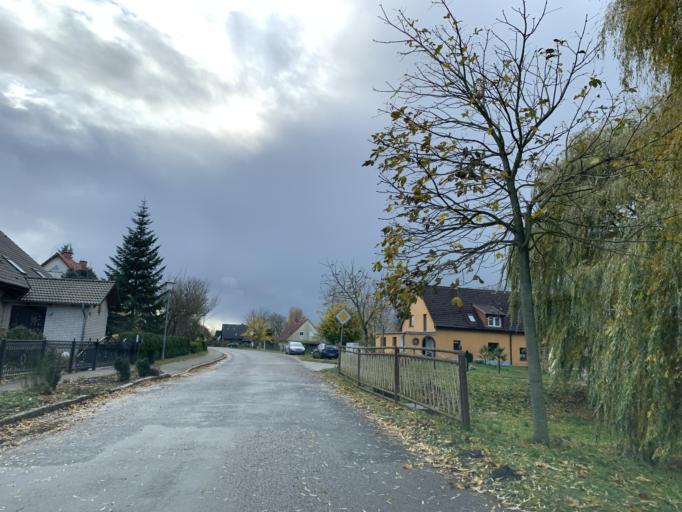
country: DE
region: Mecklenburg-Vorpommern
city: Blankensee
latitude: 53.3836
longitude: 13.2618
